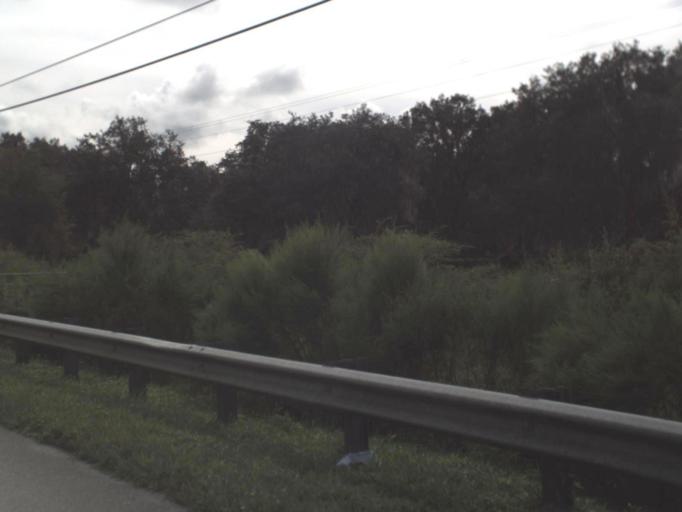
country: US
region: Florida
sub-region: Highlands County
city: Lake Placid
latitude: 27.2084
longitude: -81.2763
